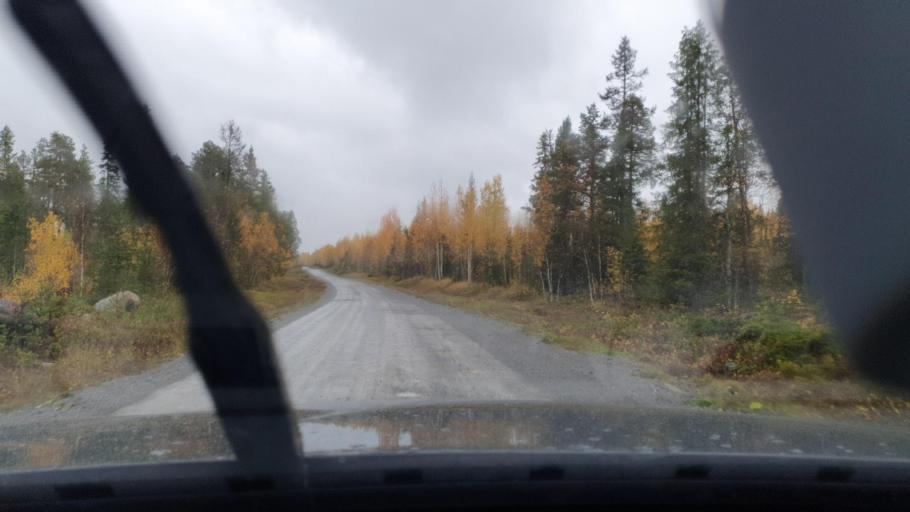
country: SE
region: Jaemtland
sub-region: Stroemsunds Kommun
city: Stroemsund
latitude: 63.5478
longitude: 15.5559
